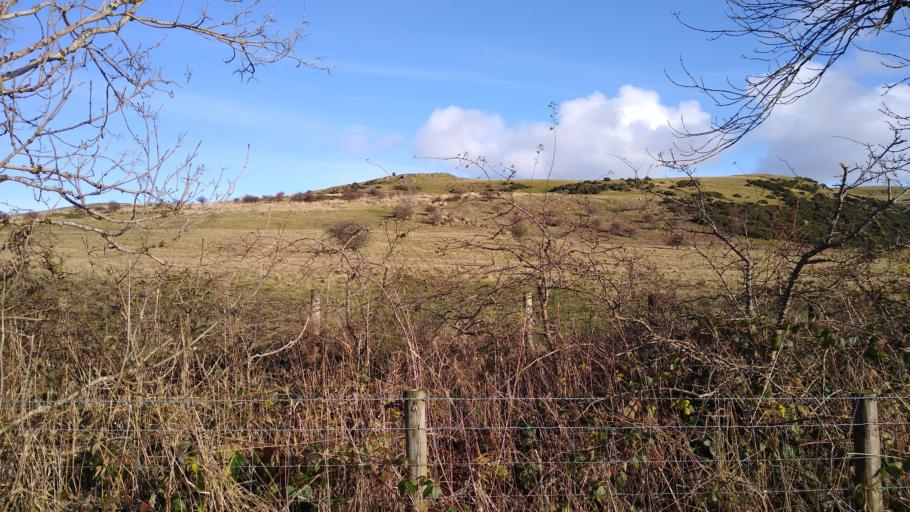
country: GB
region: England
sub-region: Cumbria
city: Aspatria
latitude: 54.7167
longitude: -3.2380
